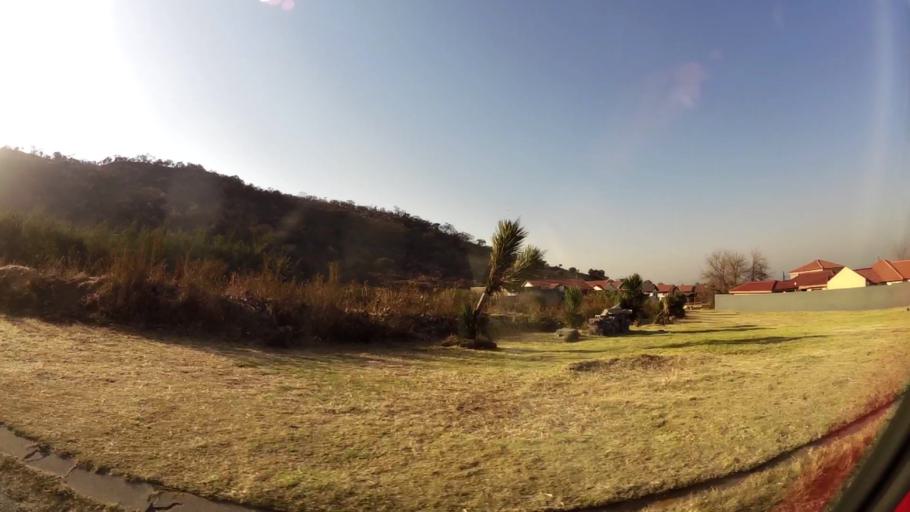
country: ZA
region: Gauteng
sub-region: City of Johannesburg Metropolitan Municipality
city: Soweto
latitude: -26.2900
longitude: 27.9612
